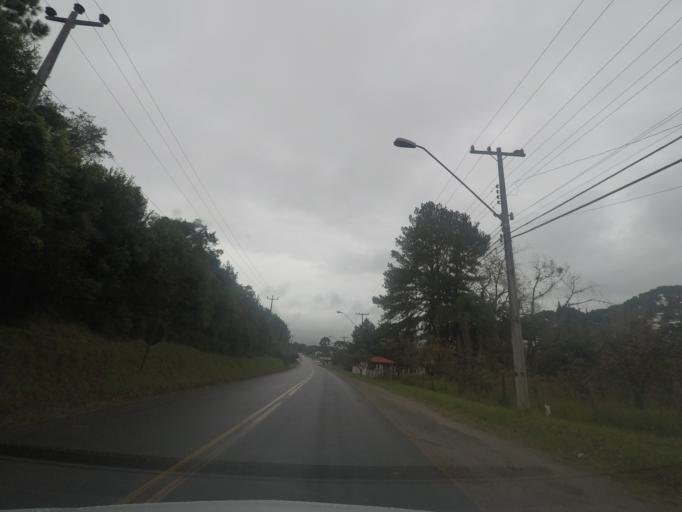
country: BR
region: Parana
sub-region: Campina Grande Do Sul
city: Campina Grande do Sul
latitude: -25.3163
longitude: -49.0745
